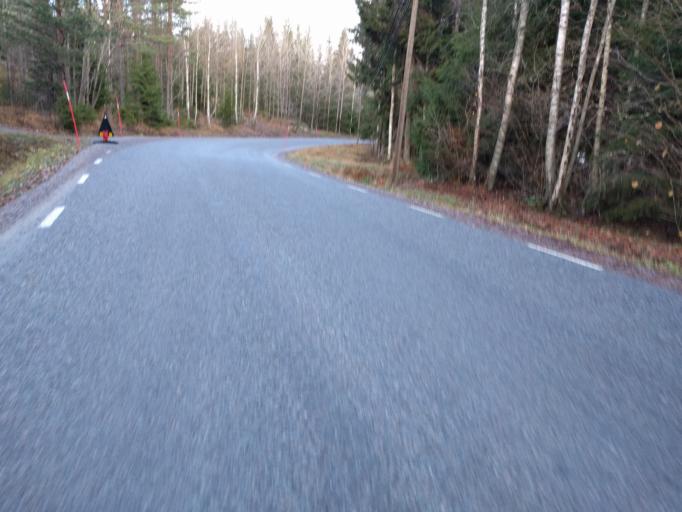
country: SE
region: Stockholm
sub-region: Osterakers Kommun
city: Akersberga
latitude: 59.5990
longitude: 18.3541
